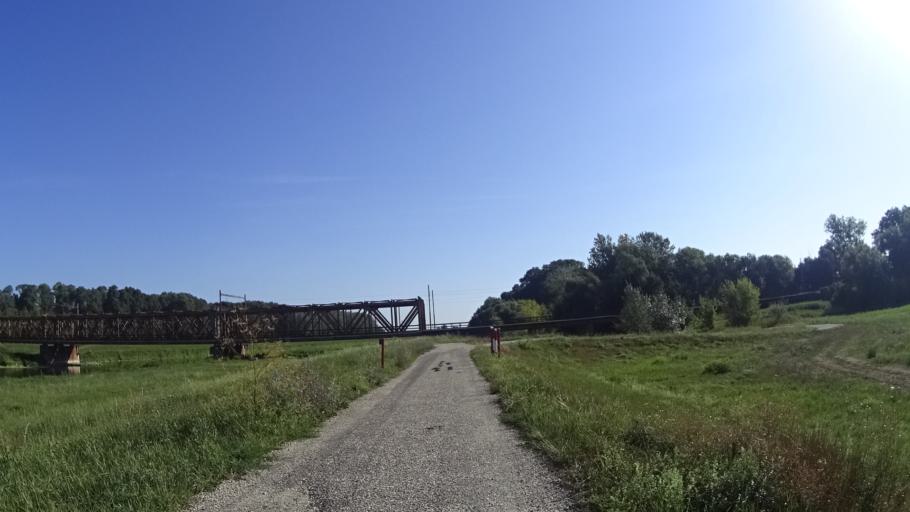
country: CZ
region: South Moravian
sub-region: Okres Breclav
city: Lanzhot
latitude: 48.7100
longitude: 16.9999
